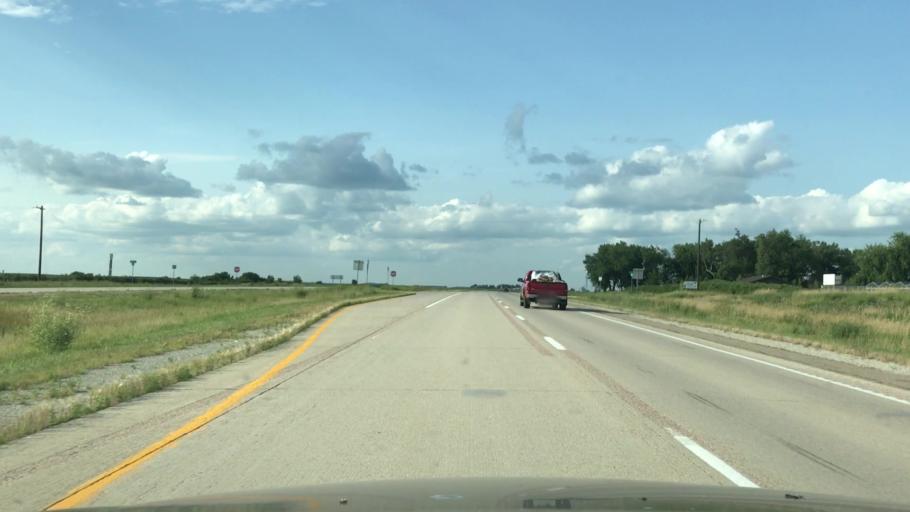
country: US
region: Iowa
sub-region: Osceola County
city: Sibley
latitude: 43.4606
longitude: -95.7124
